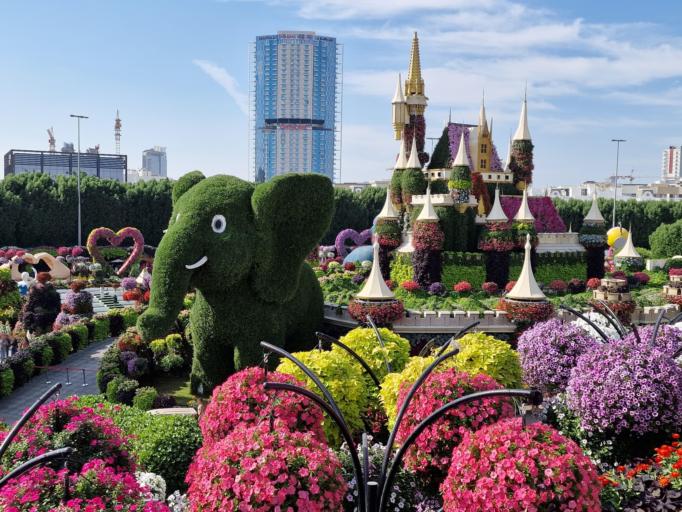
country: AE
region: Dubai
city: Dubai
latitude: 25.0597
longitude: 55.2448
